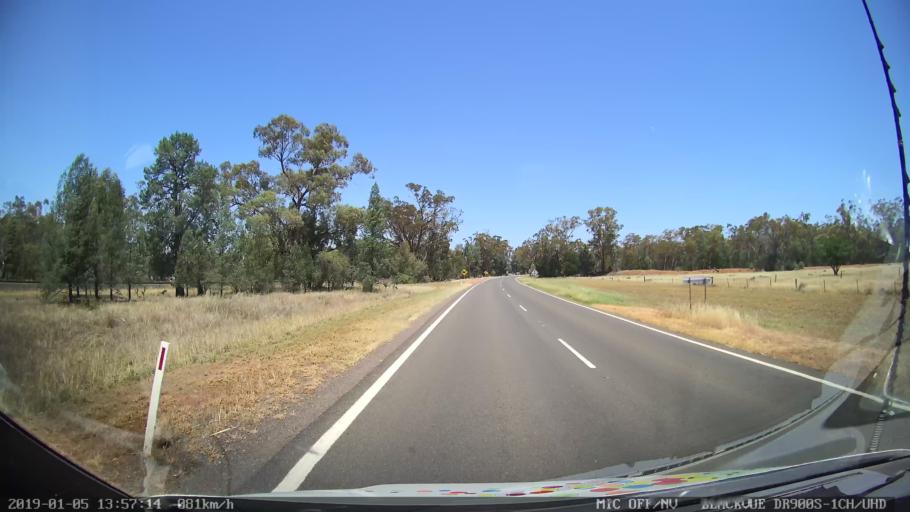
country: AU
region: New South Wales
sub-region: Gunnedah
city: Gunnedah
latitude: -31.1254
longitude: 150.2734
